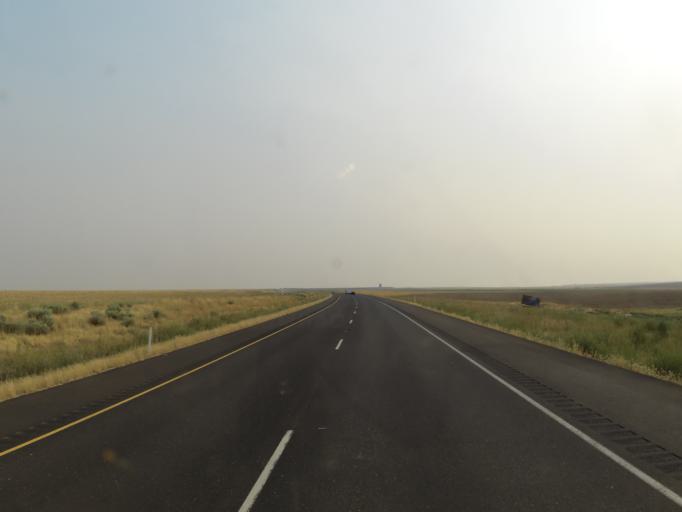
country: US
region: Washington
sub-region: Franklin County
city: Connell
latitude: 46.7189
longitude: -118.8354
